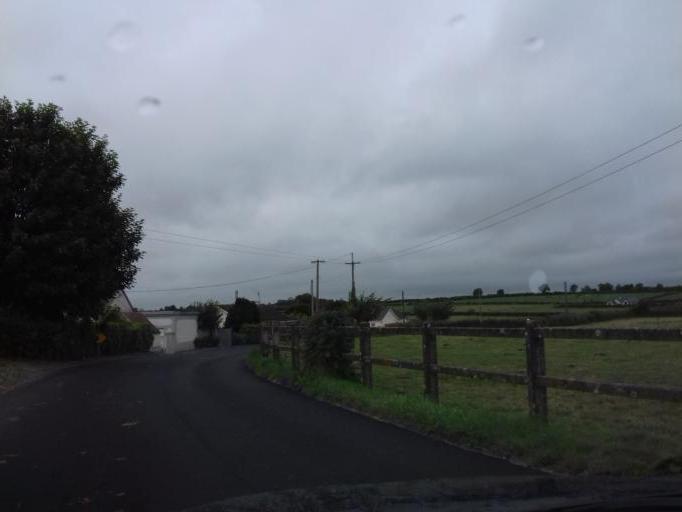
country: IE
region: Leinster
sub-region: Kilkenny
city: Graiguenamanagh
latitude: 52.6091
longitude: -7.0254
